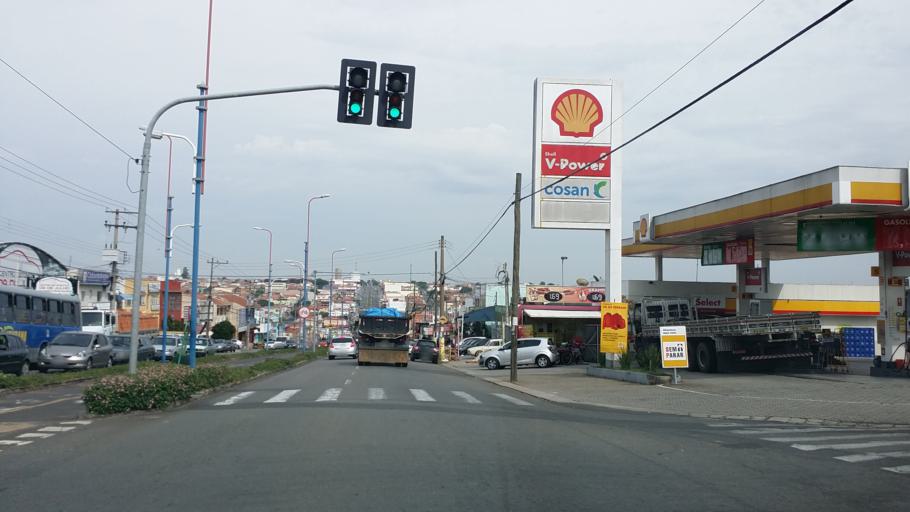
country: BR
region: Sao Paulo
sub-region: Indaiatuba
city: Indaiatuba
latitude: -23.1192
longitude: -47.2271
